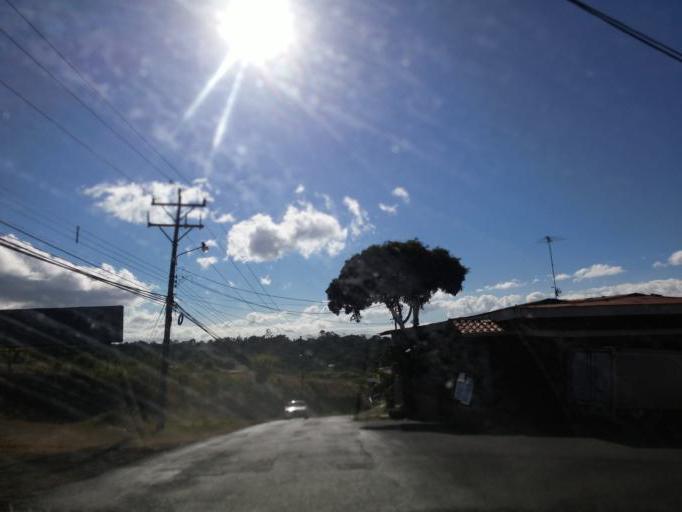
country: CR
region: Alajuela
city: Sabanilla
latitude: 10.0473
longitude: -84.2131
